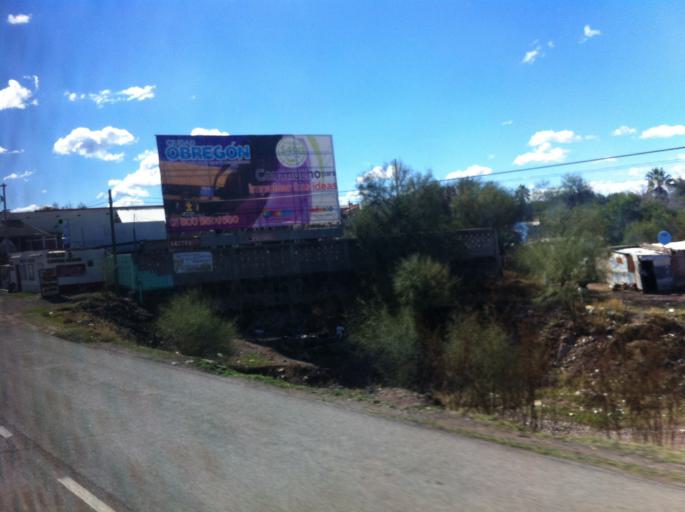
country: MX
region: Sonora
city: Santa Ana
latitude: 30.5390
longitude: -111.1142
